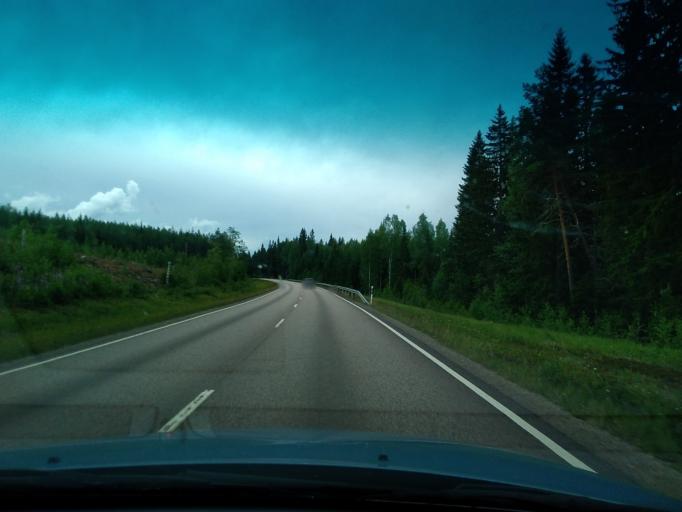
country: FI
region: Central Finland
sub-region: Keuruu
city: Multia
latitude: 62.3758
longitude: 24.7430
